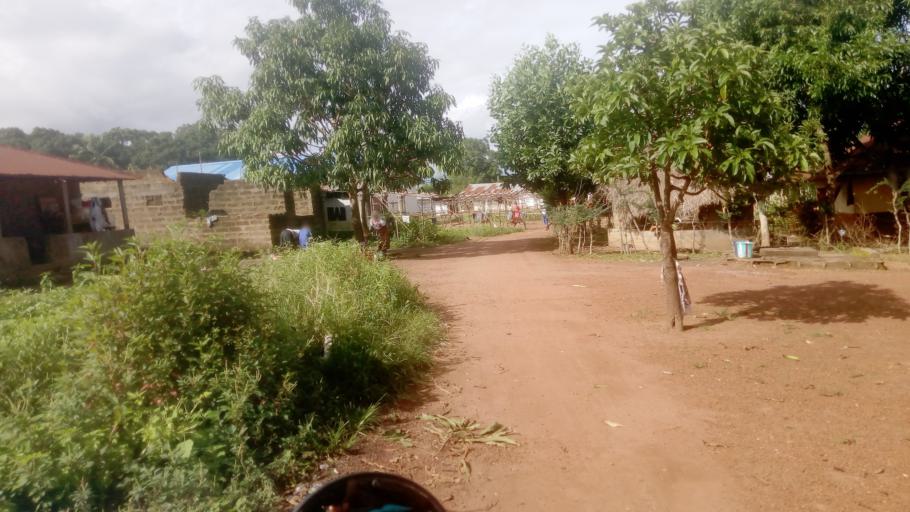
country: SL
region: Northern Province
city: Port Loko
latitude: 8.7084
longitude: -12.6790
